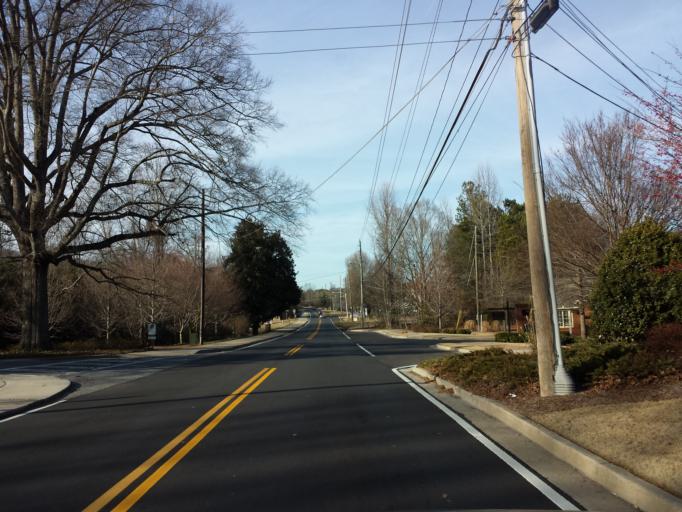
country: US
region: Georgia
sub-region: Cobb County
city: Marietta
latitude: 33.9708
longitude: -84.5637
